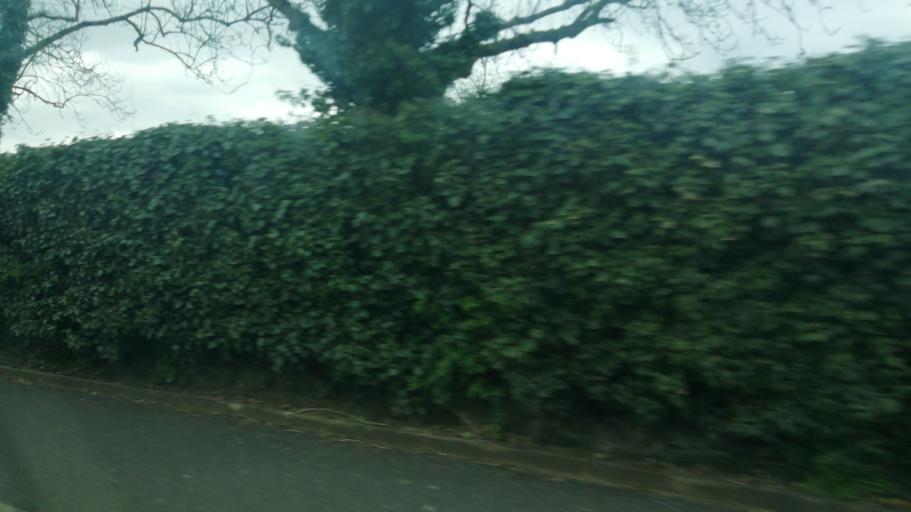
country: IE
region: Leinster
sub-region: Kildare
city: Prosperous
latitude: 53.2893
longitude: -6.7527
